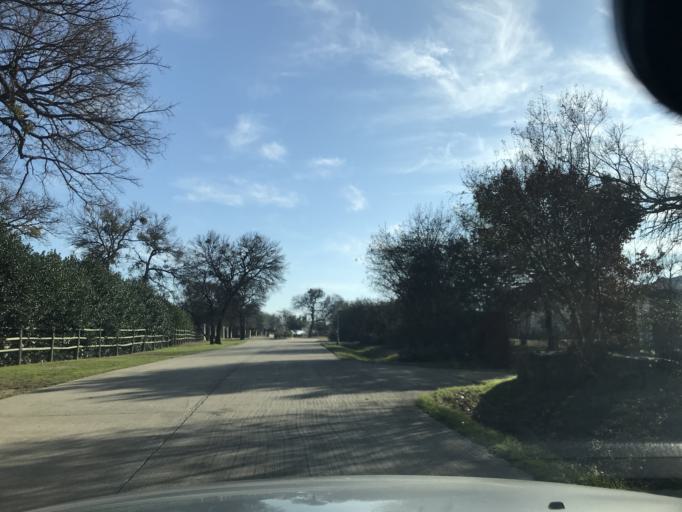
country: US
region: Texas
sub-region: Denton County
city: The Colony
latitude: 33.0929
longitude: -96.8364
